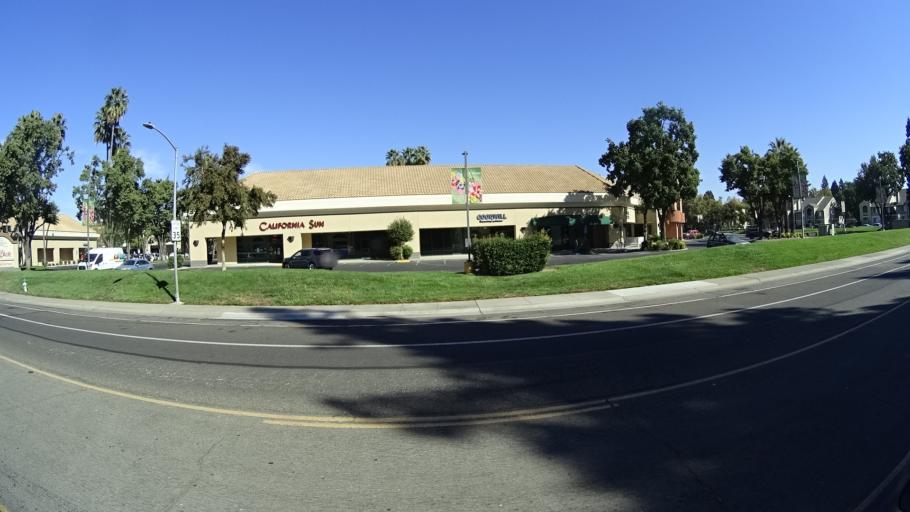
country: US
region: California
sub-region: Sacramento County
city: Parkway
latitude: 38.4849
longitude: -121.5349
